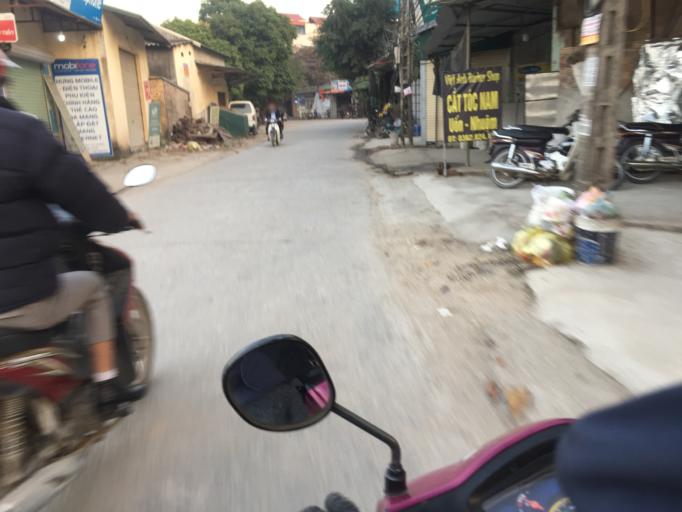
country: VN
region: Ha Noi
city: Chuc Son
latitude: 20.8931
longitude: 105.7229
